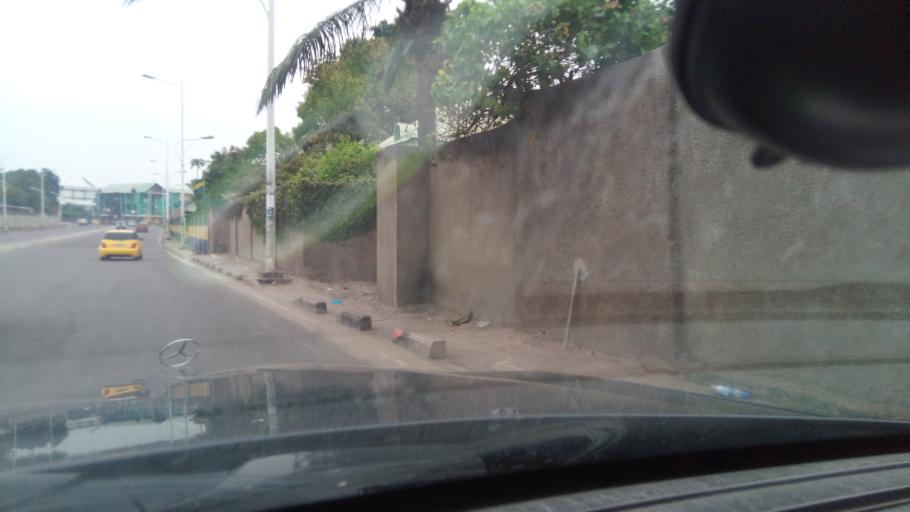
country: CD
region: Kinshasa
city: Kinshasa
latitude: -4.3334
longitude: 15.2597
